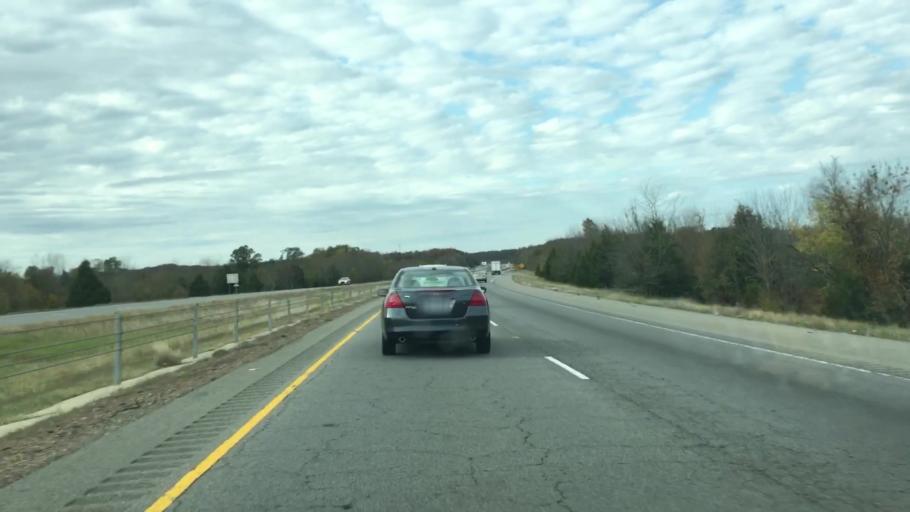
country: US
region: Arkansas
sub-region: Faulkner County
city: Conway
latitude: 35.1269
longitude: -92.5111
